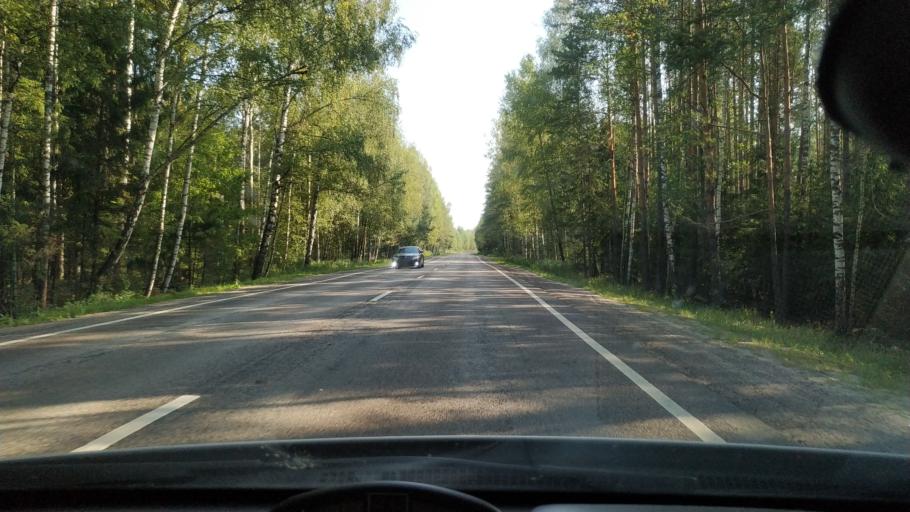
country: RU
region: Moskovskaya
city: Dmitrovskiy Pogost
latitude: 55.2300
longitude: 39.9437
